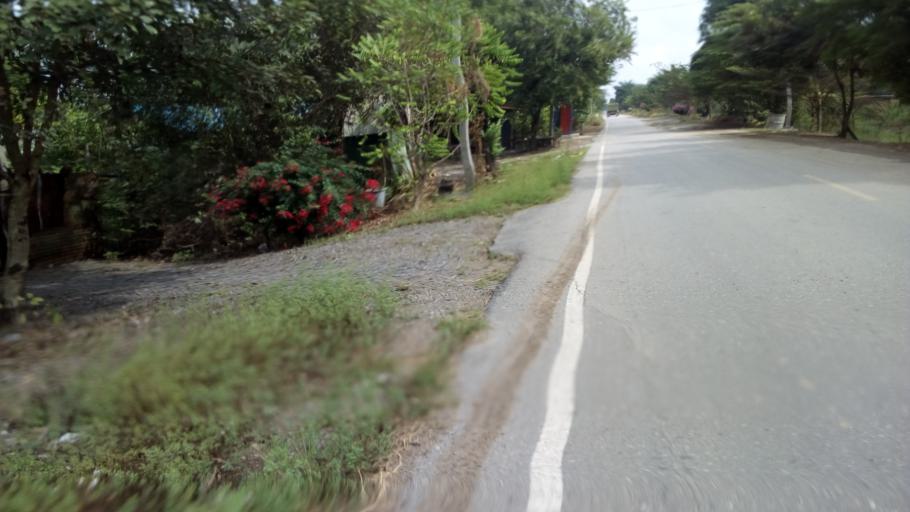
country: TH
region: Sara Buri
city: Nong Khae
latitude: 14.2452
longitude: 100.8265
